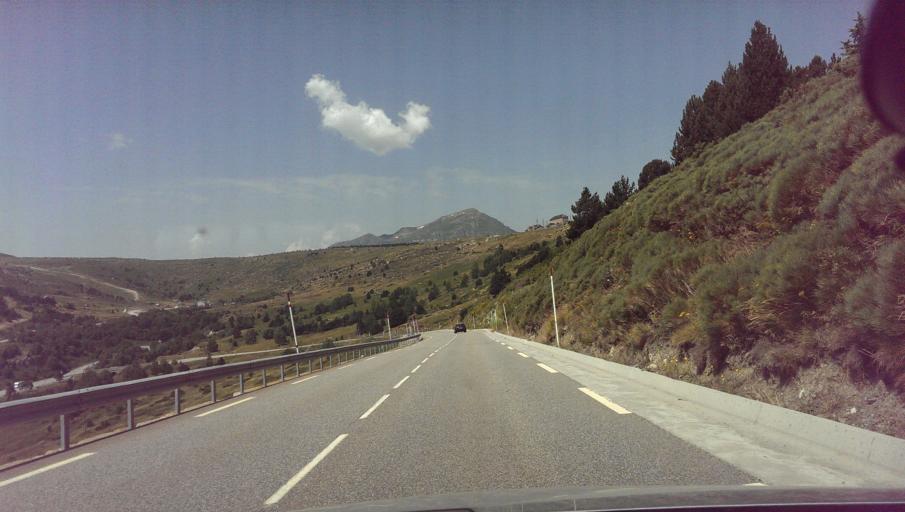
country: AD
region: Encamp
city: Pas de la Casa
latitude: 42.5551
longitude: 1.8202
